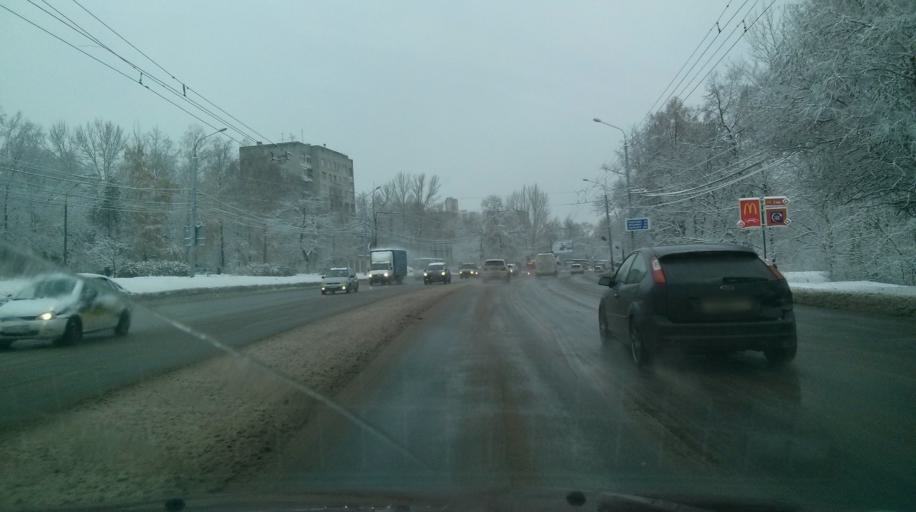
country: RU
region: Nizjnij Novgorod
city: Nizhniy Novgorod
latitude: 56.2424
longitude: 43.9640
